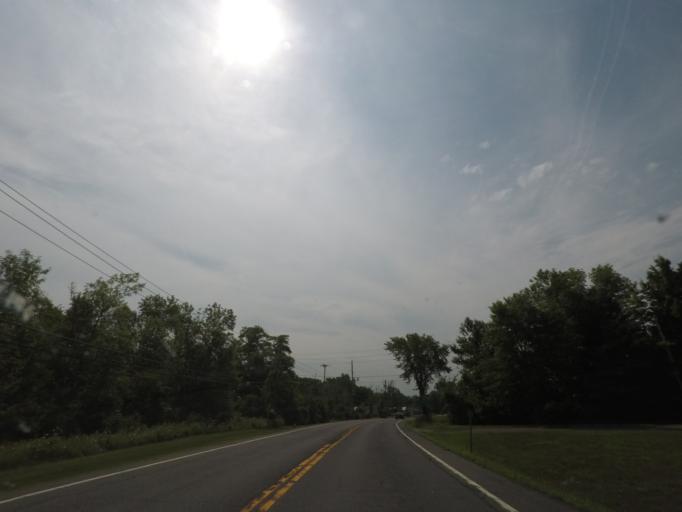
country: US
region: New York
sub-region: Saratoga County
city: Mechanicville
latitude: 42.8757
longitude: -73.6797
